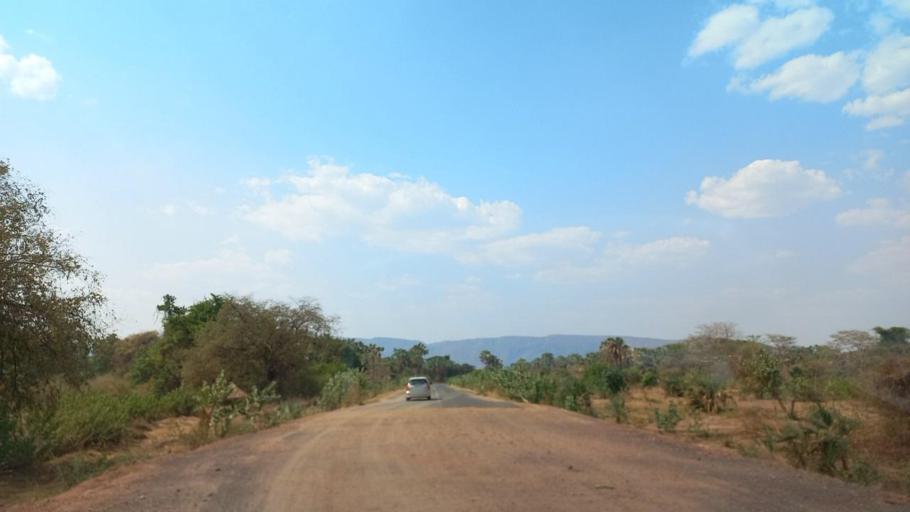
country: ZM
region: Lusaka
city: Luangwa
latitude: -15.0934
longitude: 30.1928
